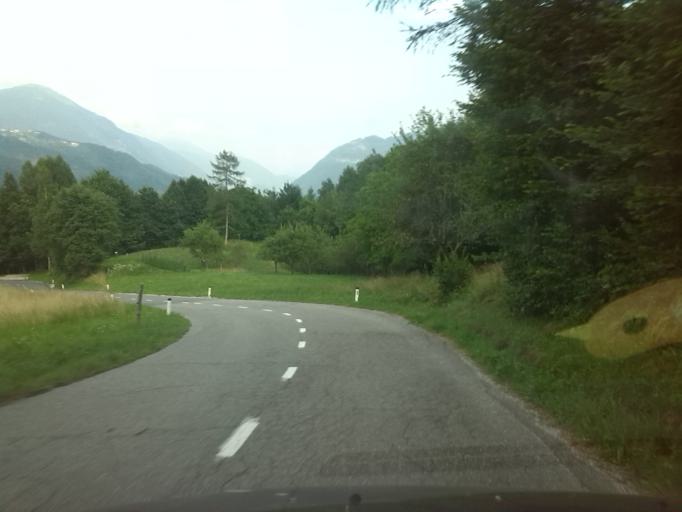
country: SI
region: Kobarid
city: Kobarid
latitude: 46.2243
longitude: 13.5913
